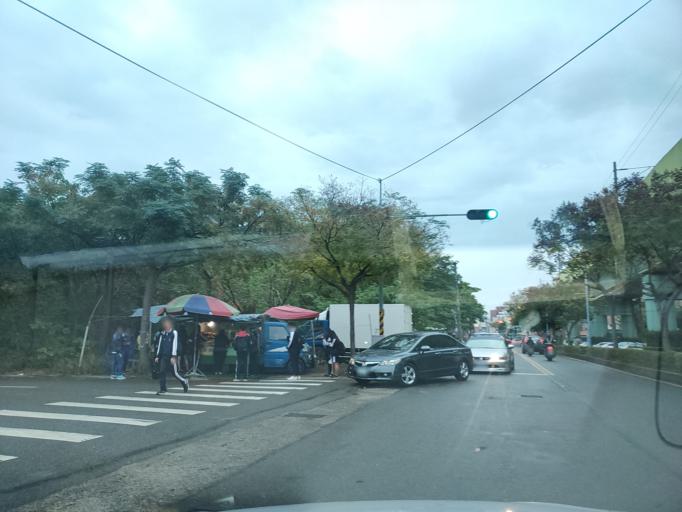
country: TW
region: Taiwan
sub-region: Miaoli
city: Miaoli
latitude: 24.5577
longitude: 120.8168
